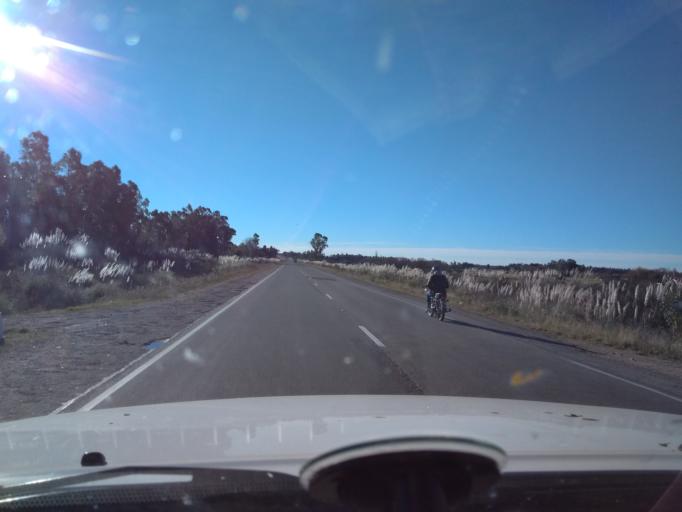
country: UY
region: Canelones
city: Sauce
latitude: -34.6051
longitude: -56.0490
